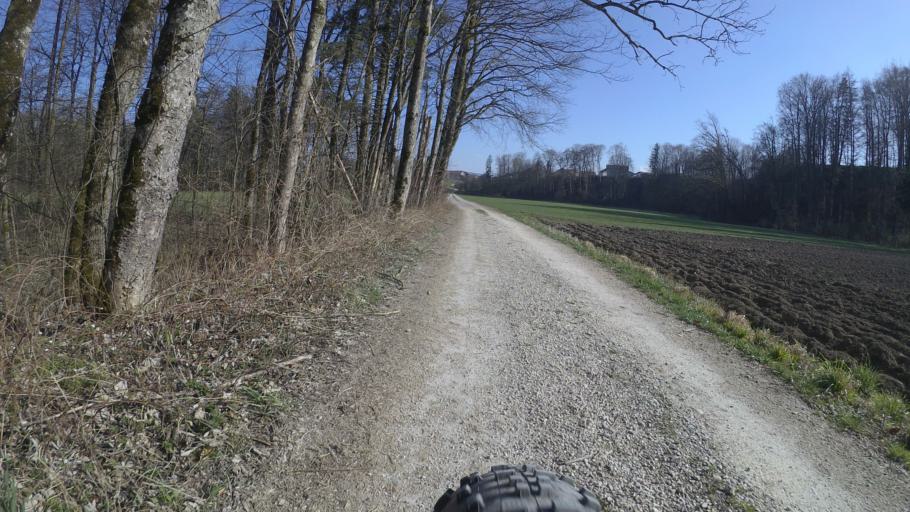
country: DE
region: Bavaria
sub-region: Upper Bavaria
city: Nussdorf
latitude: 47.9259
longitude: 12.6100
